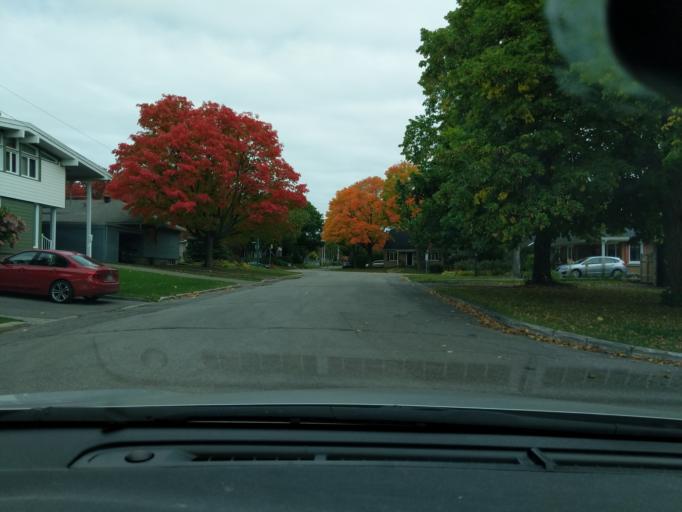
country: CA
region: Quebec
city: Quebec
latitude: 46.7681
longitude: -71.2757
